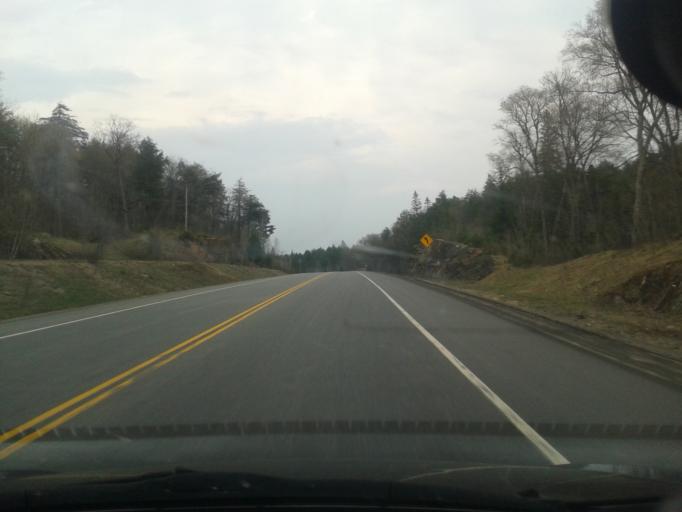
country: CA
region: Ontario
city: Huntsville
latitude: 45.5192
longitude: -78.7151
